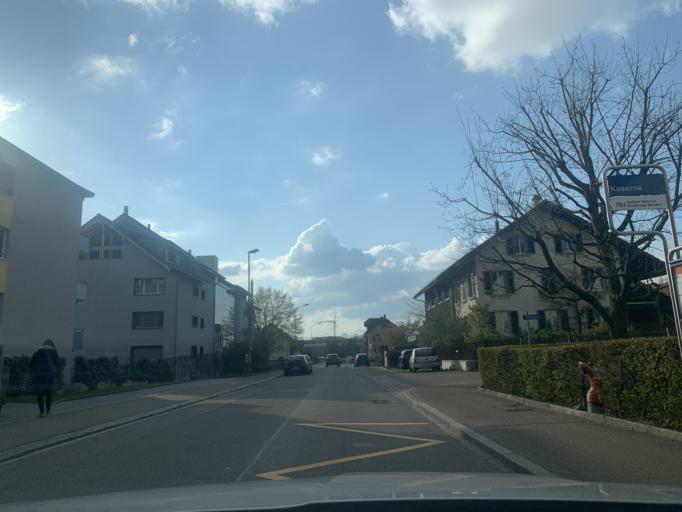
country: CH
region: Zurich
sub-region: Bezirk Buelach
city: Wallisellen / Wallisellen-West
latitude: 47.4170
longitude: 8.5854
